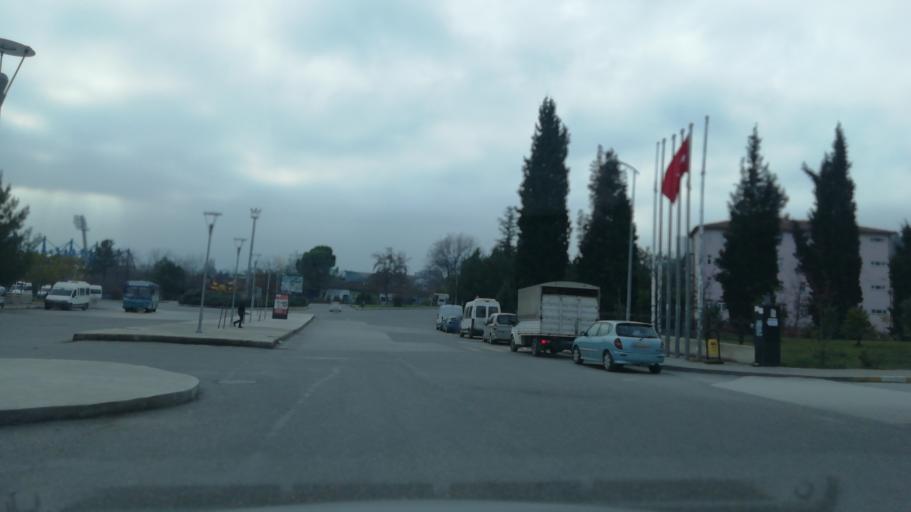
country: TR
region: Karabuk
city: Karabuk
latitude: 41.2079
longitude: 32.6196
